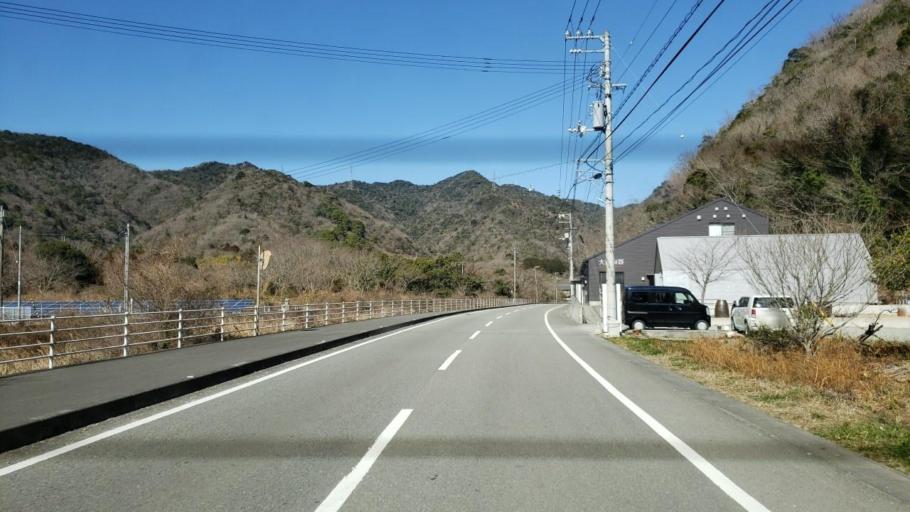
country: JP
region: Tokushima
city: Narutocho-mitsuishi
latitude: 34.1680
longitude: 134.5409
